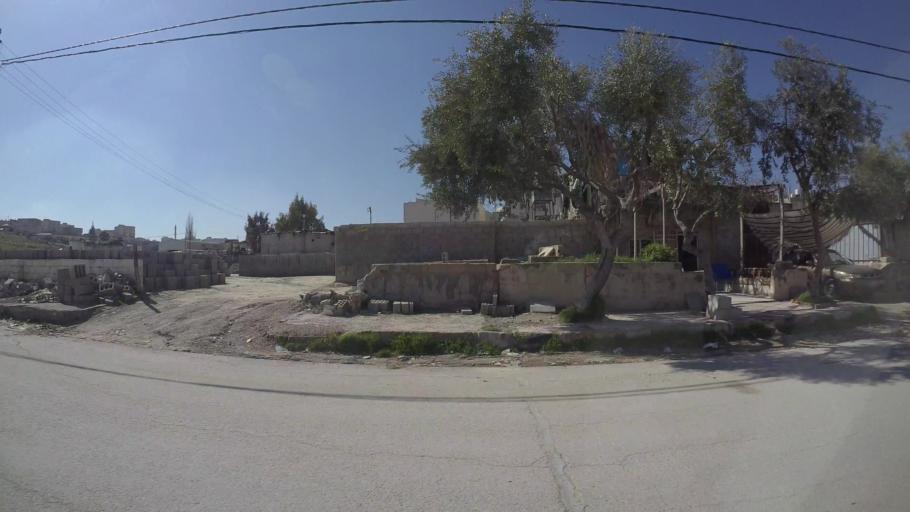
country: JO
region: Amman
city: Al Bunayyat ash Shamaliyah
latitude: 31.9112
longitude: 35.9091
